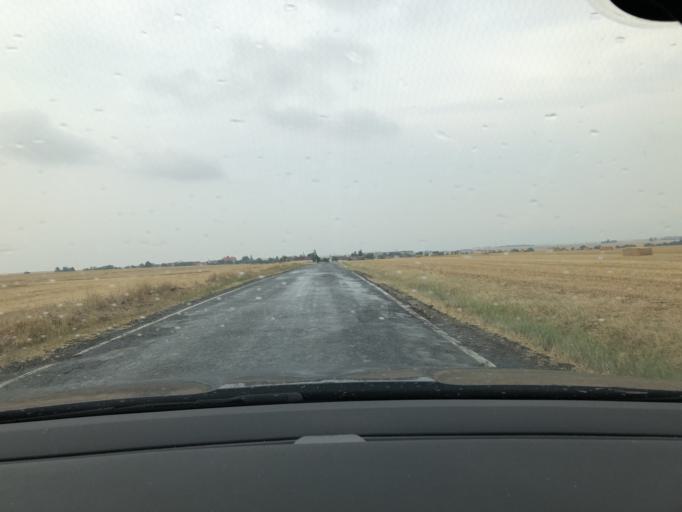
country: CZ
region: South Moravian
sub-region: Okres Znojmo
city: Jevisovice
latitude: 49.0271
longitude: 16.0404
